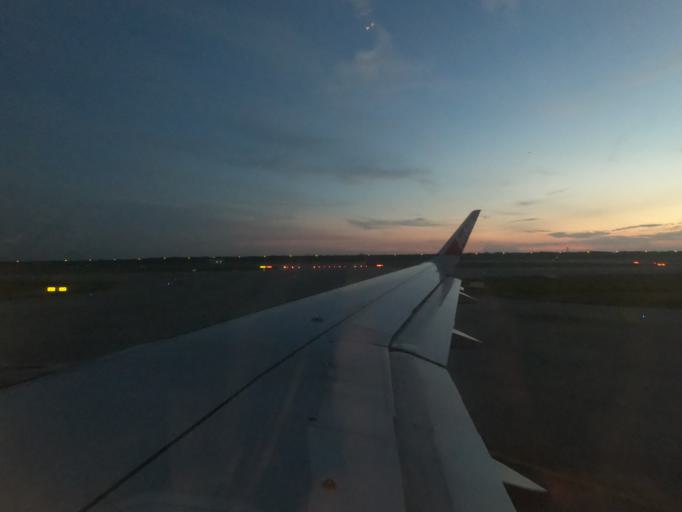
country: MY
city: Sungai Pelek New Village
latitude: 2.7357
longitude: 101.6825
